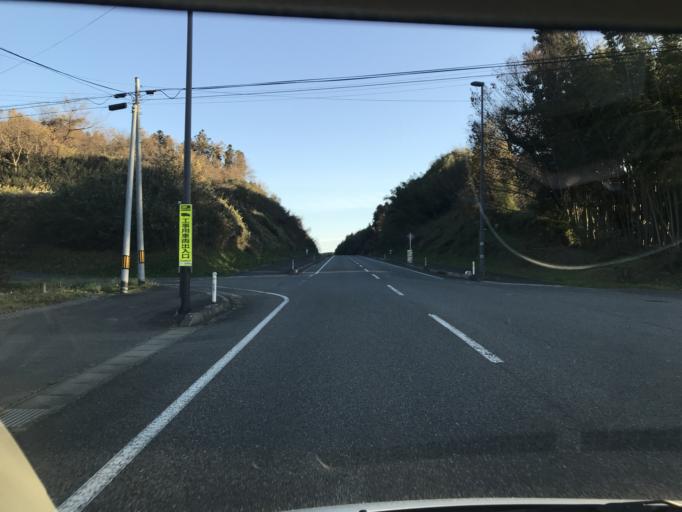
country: JP
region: Iwate
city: Ichinoseki
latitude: 38.9583
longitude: 141.1747
